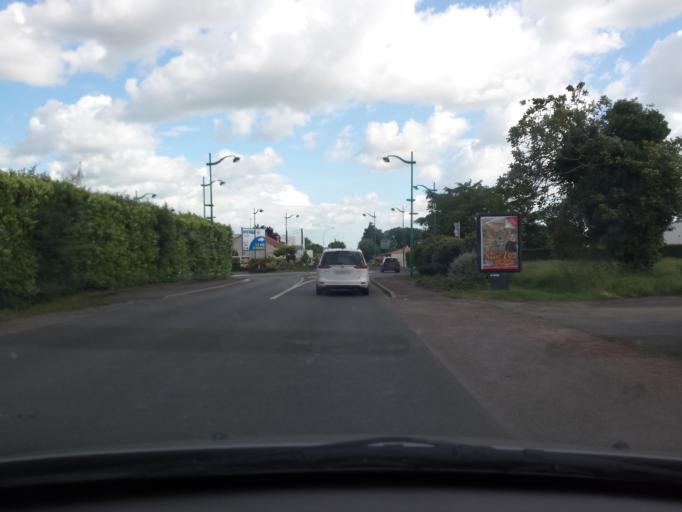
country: FR
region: Pays de la Loire
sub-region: Departement de la Vendee
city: Lucon
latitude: 46.4681
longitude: -1.1746
